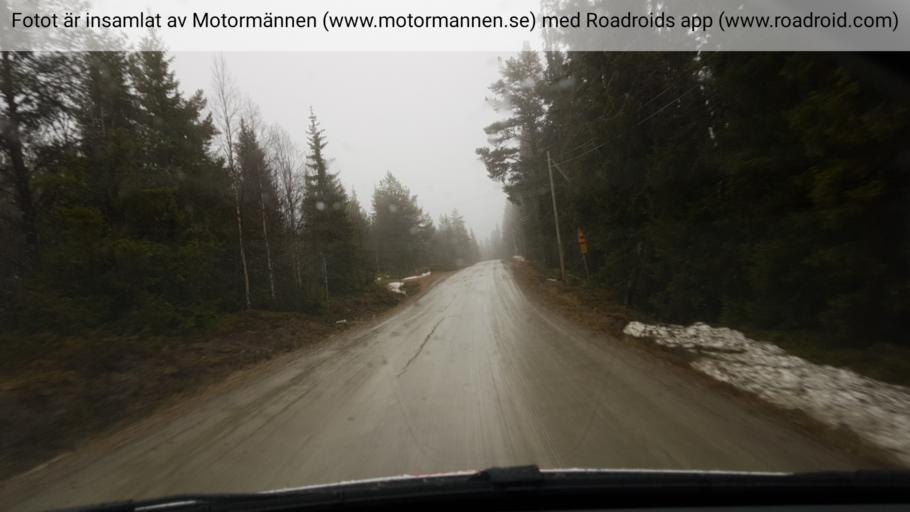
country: SE
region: Jaemtland
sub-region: Are Kommun
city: Jarpen
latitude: 62.5857
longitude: 13.3802
